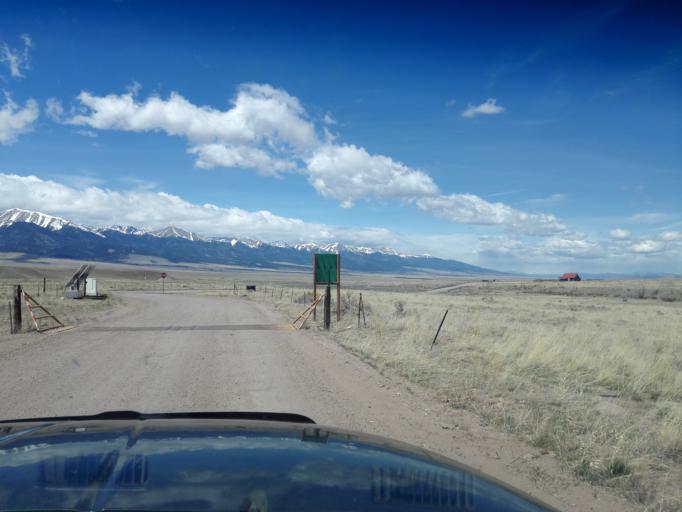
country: US
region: Colorado
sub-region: Custer County
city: Westcliffe
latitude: 37.9936
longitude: -105.3579
